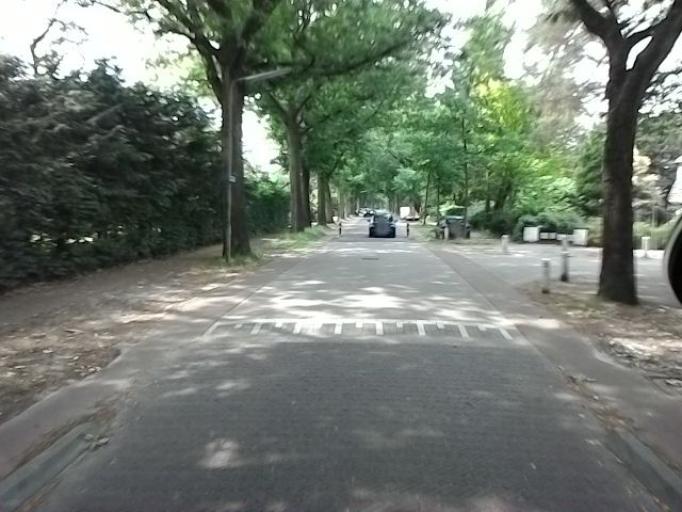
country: NL
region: Utrecht
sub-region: Gemeente Zeist
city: Zeist
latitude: 52.1325
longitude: 5.2279
